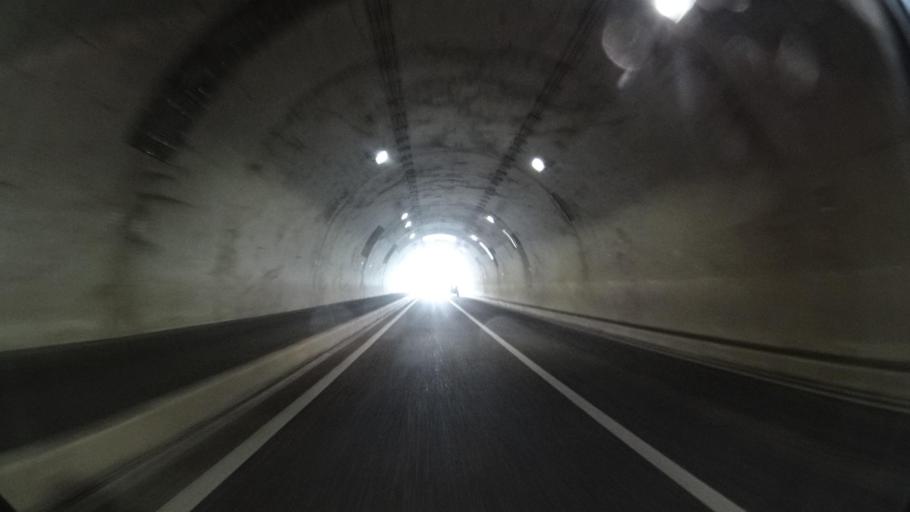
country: JP
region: Kyoto
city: Maizuru
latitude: 35.5338
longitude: 135.3472
